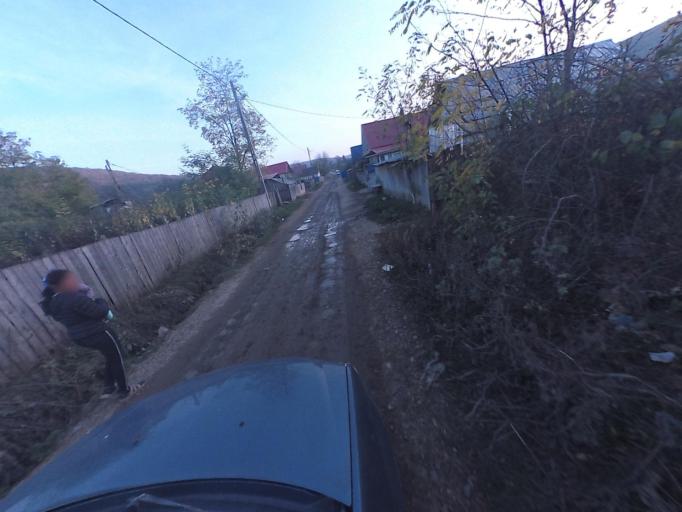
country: RO
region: Vaslui
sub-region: Comuna Garceni
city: Garceni
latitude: 46.7905
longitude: 27.2434
